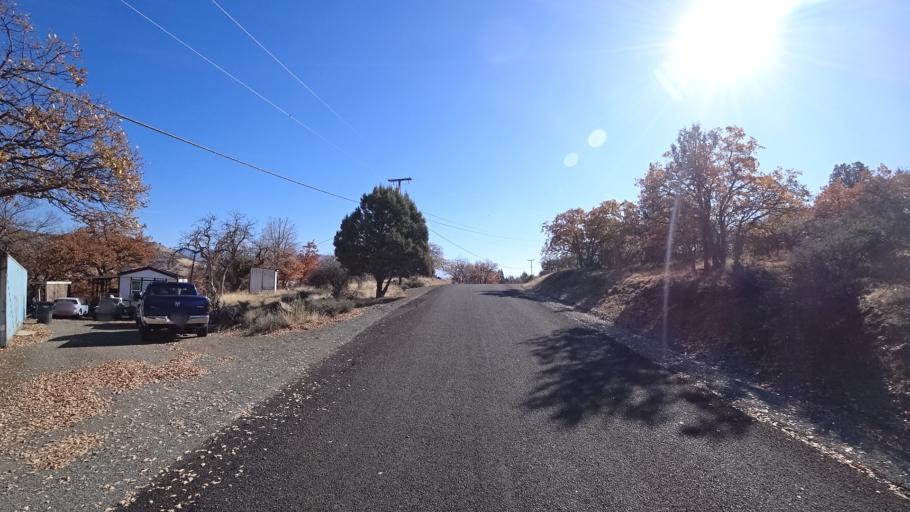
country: US
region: California
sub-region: Siskiyou County
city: Montague
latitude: 41.8798
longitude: -122.4831
